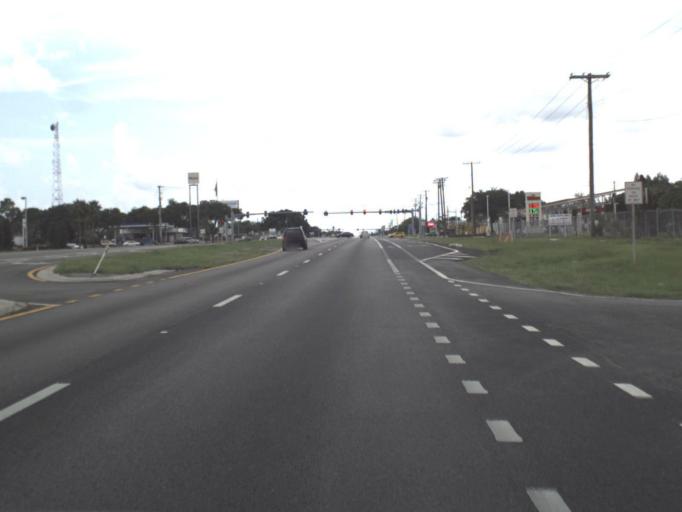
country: US
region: Florida
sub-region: Hillsborough County
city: East Lake-Orient Park
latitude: 27.9963
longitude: -82.3706
